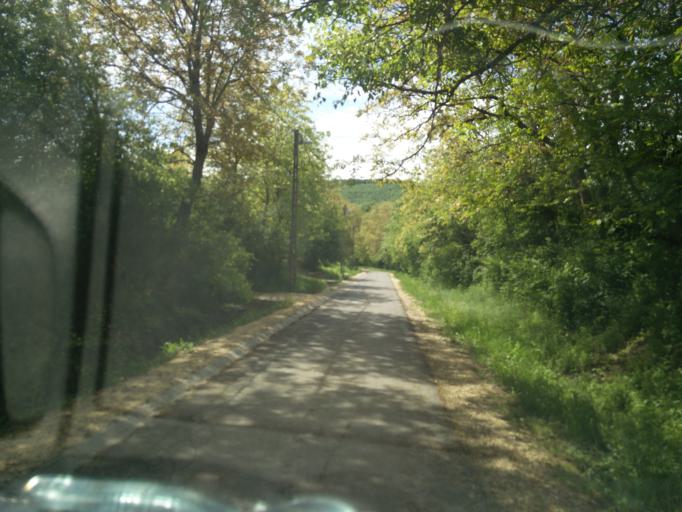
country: HU
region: Tolna
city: Szentgalpuszta
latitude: 46.2766
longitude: 18.6375
